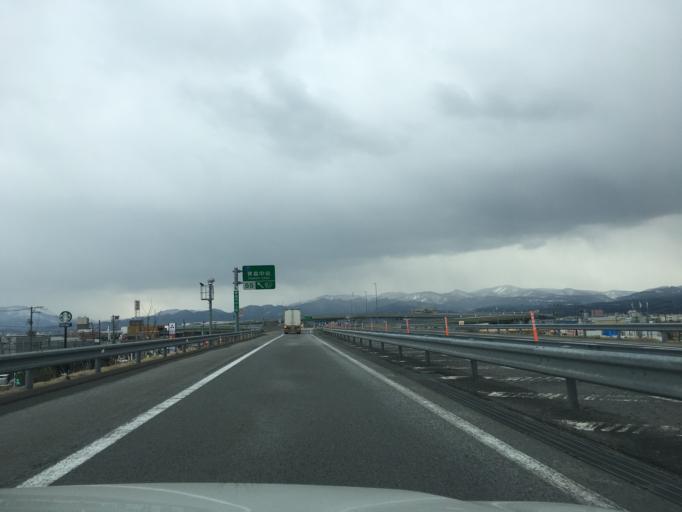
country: JP
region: Aomori
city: Aomori Shi
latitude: 40.7969
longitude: 140.7378
